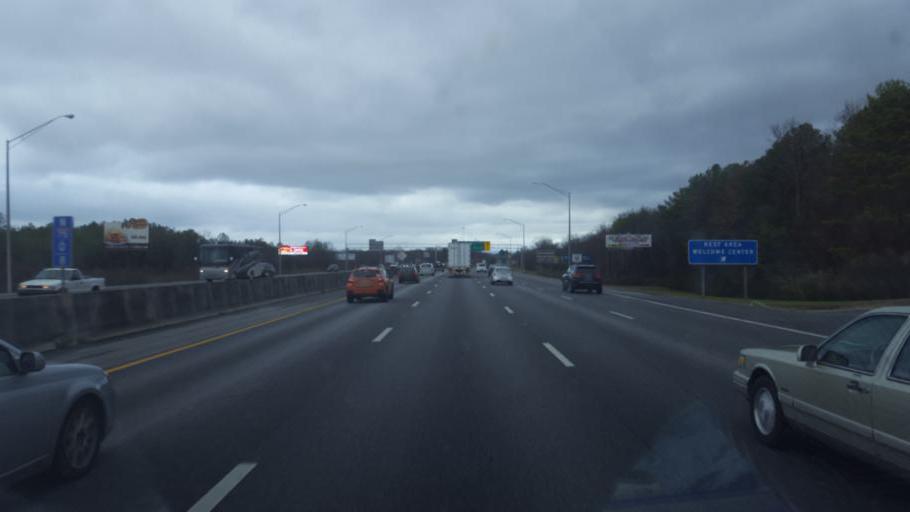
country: US
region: Tennessee
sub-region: Hamilton County
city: East Ridge
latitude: 34.9960
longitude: -85.2078
